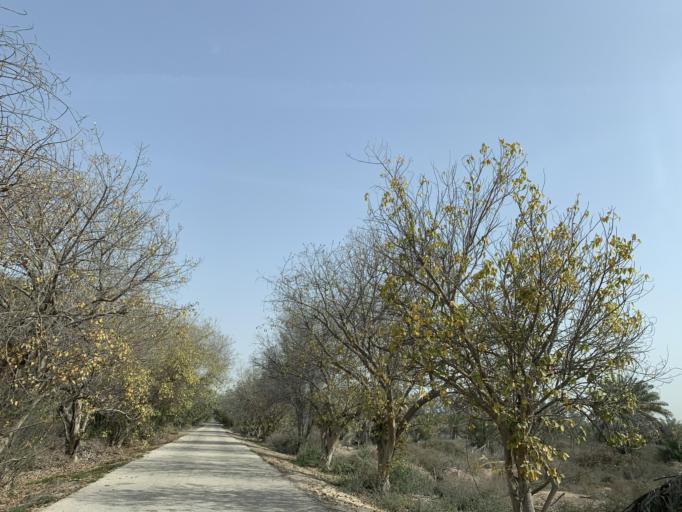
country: BH
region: Northern
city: Madinat `Isa
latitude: 26.1631
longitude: 50.5310
